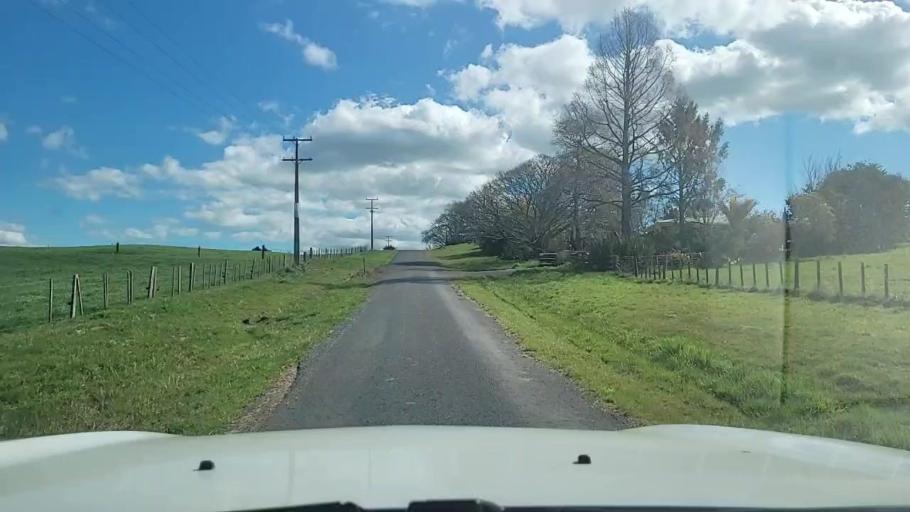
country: NZ
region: Waikato
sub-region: Hauraki District
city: Paeroa
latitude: -37.5742
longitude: 175.4772
